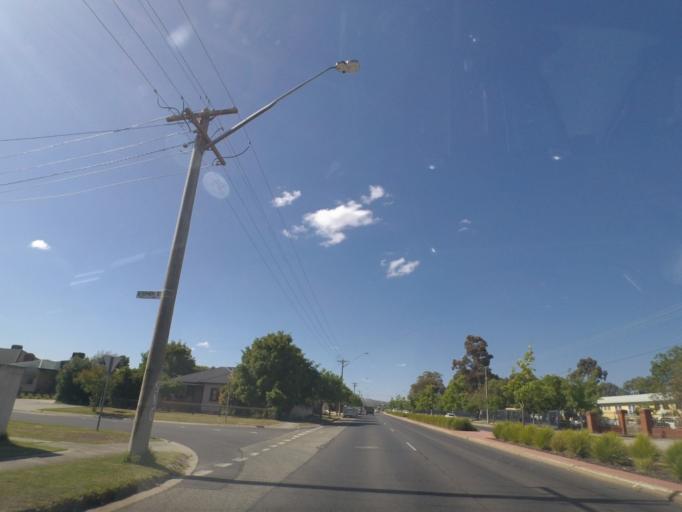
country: AU
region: New South Wales
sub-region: Albury Municipality
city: North Albury
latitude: -36.0654
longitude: 146.9310
